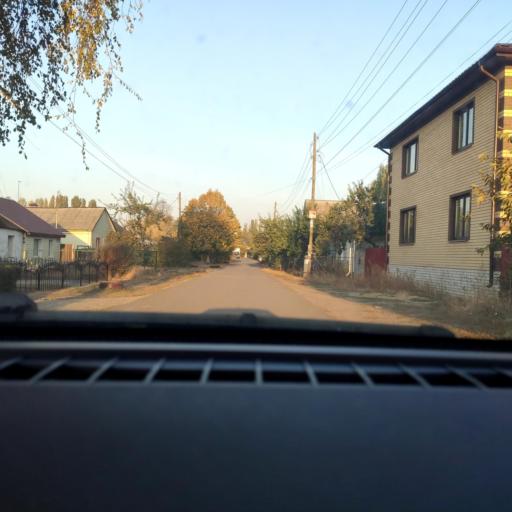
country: RU
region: Voronezj
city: Maslovka
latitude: 51.6328
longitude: 39.2765
